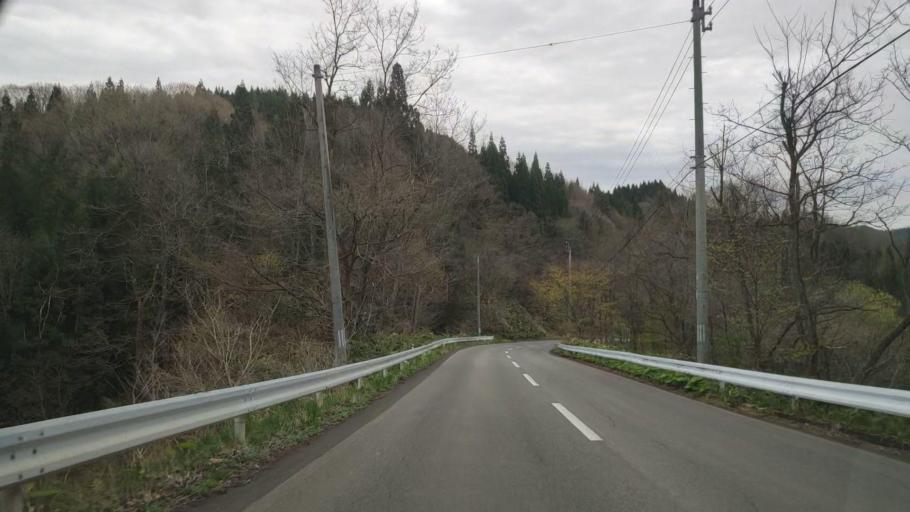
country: JP
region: Akita
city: Hanawa
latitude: 40.3683
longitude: 140.7838
